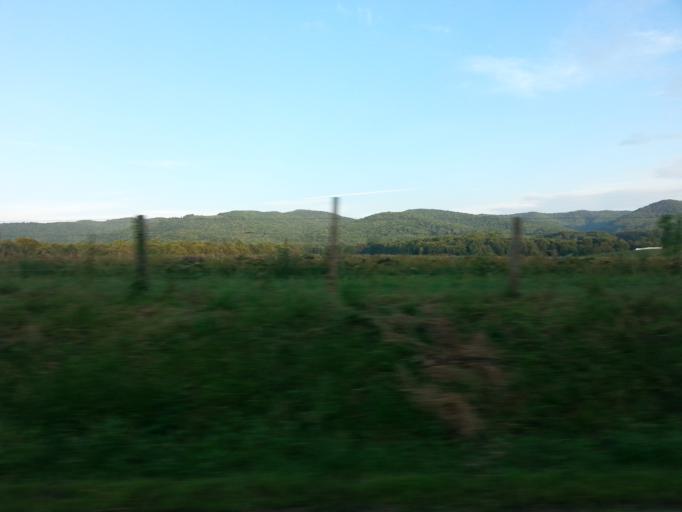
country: US
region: Tennessee
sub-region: Johnson County
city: Mountain City
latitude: 36.5101
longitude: -81.9394
